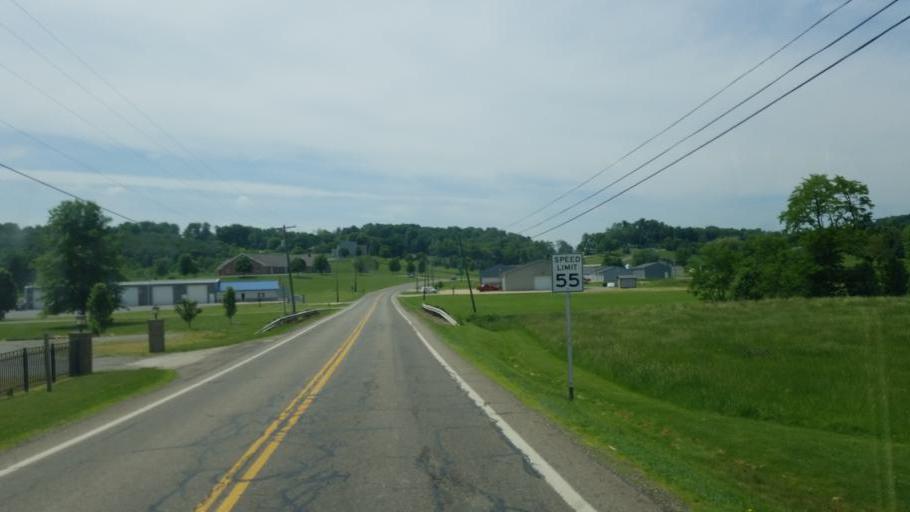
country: US
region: Ohio
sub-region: Tuscarawas County
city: Sugarcreek
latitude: 40.4998
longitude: -81.6610
